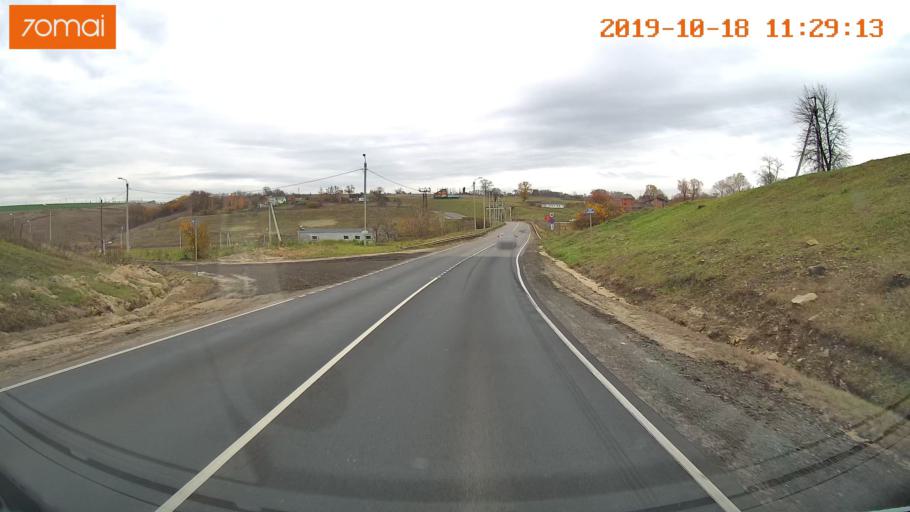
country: RU
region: Rjazan
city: Oktyabr'skiy
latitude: 54.1573
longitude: 38.6741
